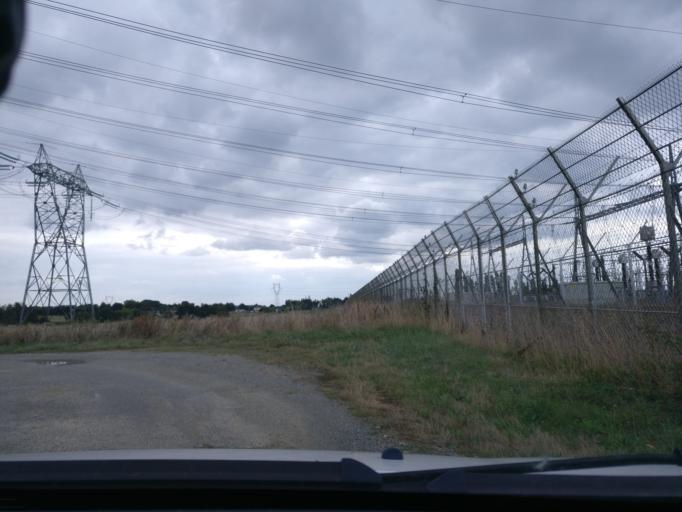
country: FR
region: Brittany
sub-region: Departement d'Ille-et-Vilaine
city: Noyal-sur-Vilaine
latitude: 48.0935
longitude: -1.5537
